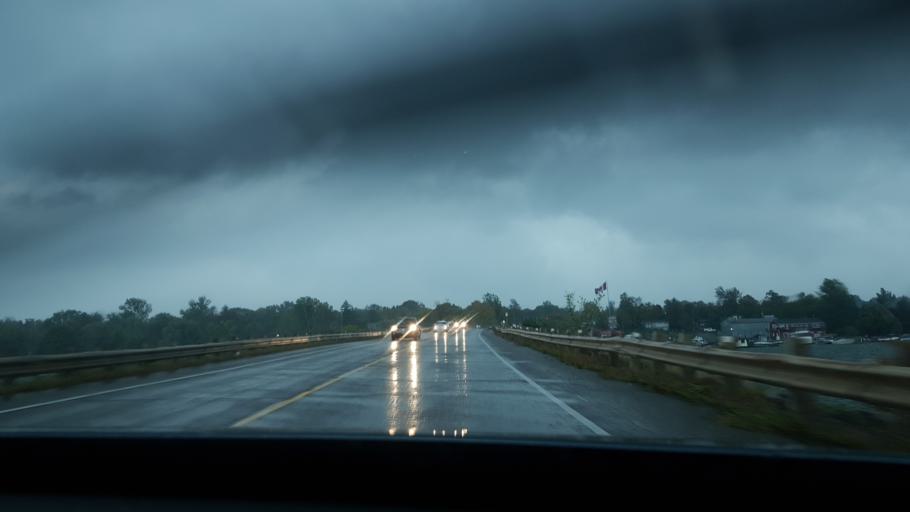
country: CA
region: Ontario
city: Peterborough
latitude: 44.3865
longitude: -78.3890
